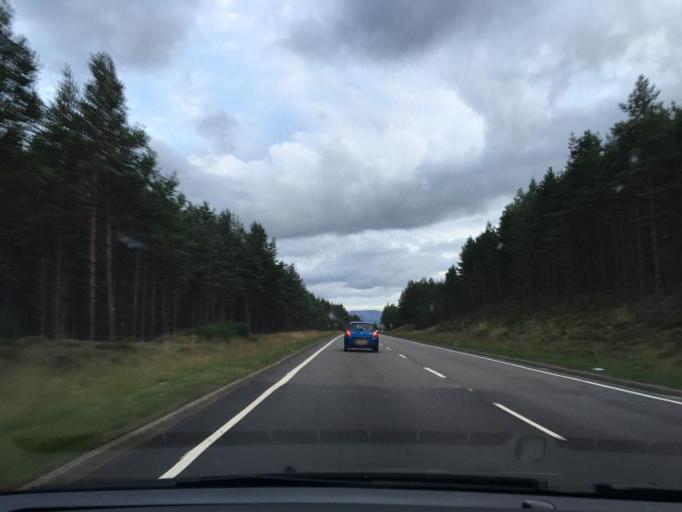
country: GB
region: Scotland
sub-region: Highland
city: Aviemore
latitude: 57.2602
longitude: -3.8104
